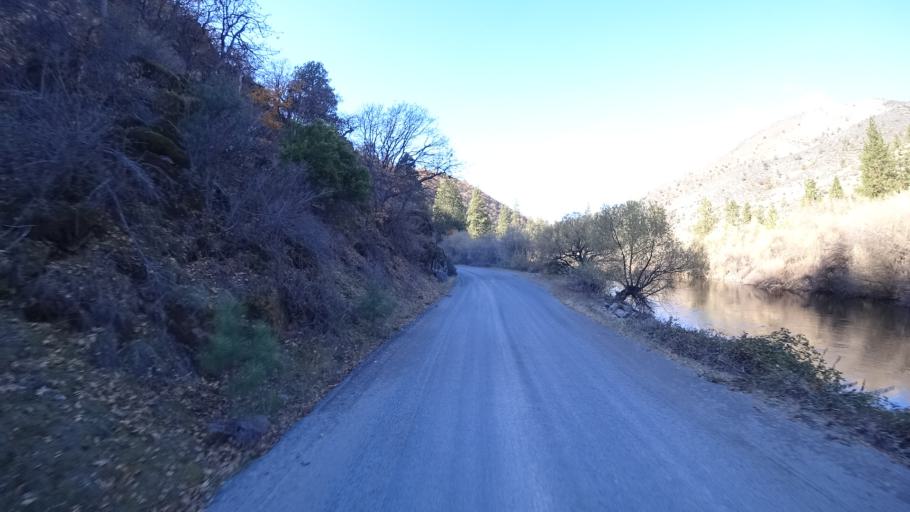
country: US
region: California
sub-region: Siskiyou County
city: Yreka
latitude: 41.8271
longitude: -122.6462
